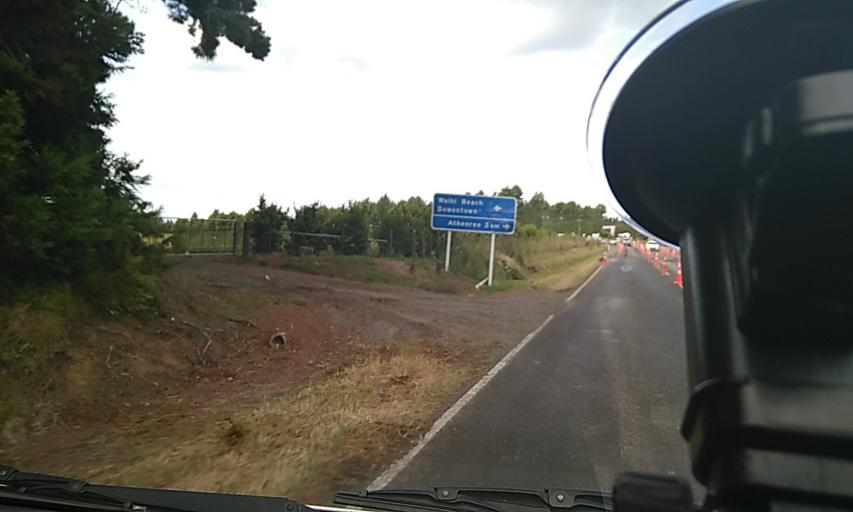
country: NZ
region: Bay of Plenty
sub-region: Western Bay of Plenty District
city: Waihi Beach
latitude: -37.4522
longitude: 175.9450
